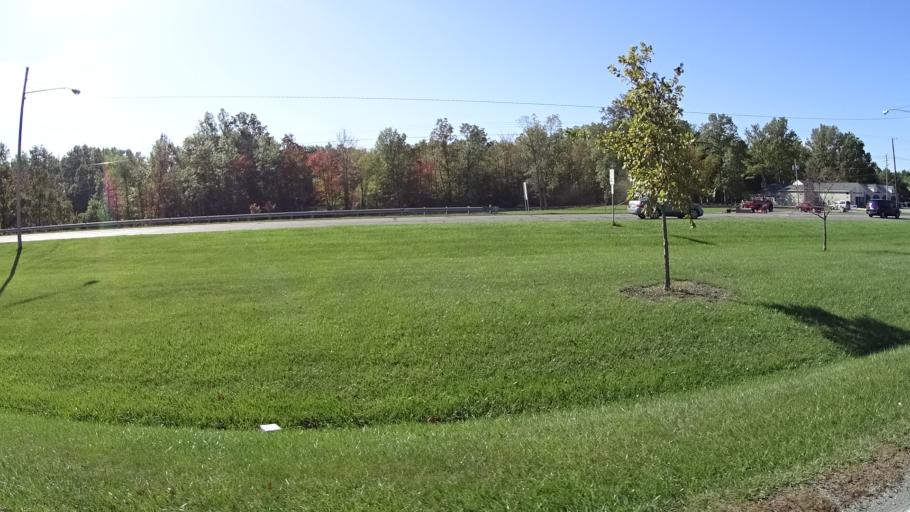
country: US
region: Ohio
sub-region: Lorain County
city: Vermilion-on-the-Lake
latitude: 41.4253
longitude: -82.3343
